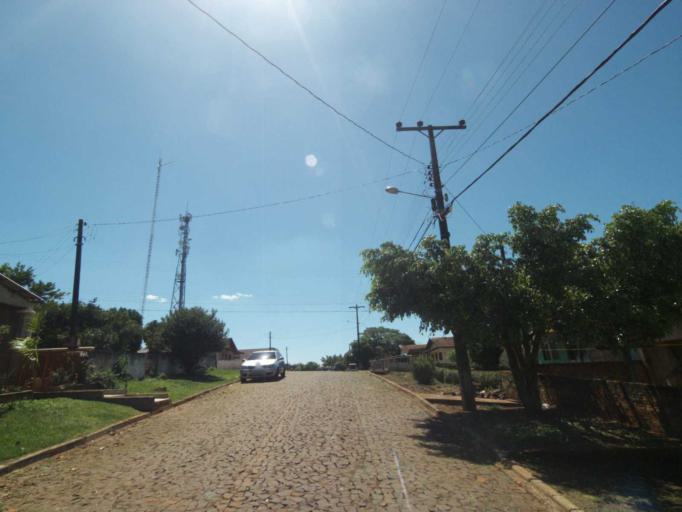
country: BR
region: Parana
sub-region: Laranjeiras Do Sul
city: Laranjeiras do Sul
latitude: -25.3883
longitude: -52.2144
